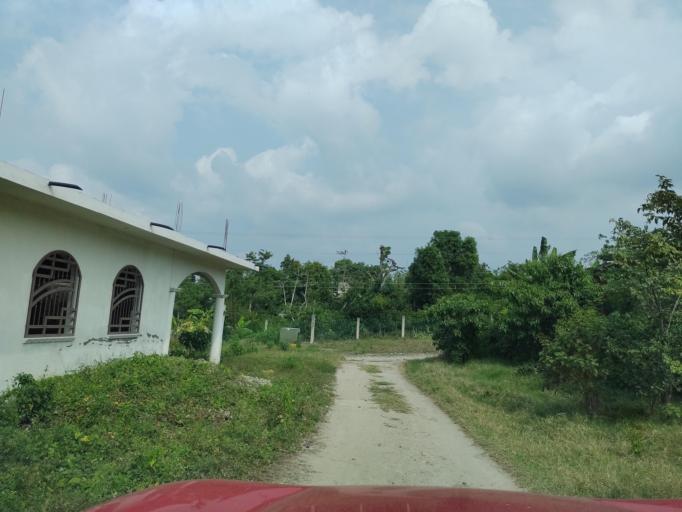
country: MX
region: Veracruz
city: Agua Dulce
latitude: 20.3631
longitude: -97.2981
